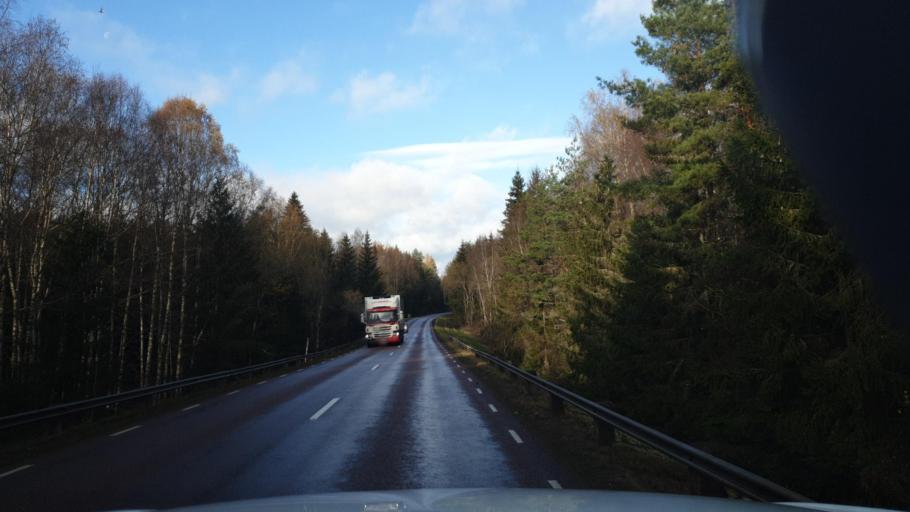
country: SE
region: Vaermland
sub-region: Grums Kommun
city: Grums
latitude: 59.4036
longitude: 13.0114
